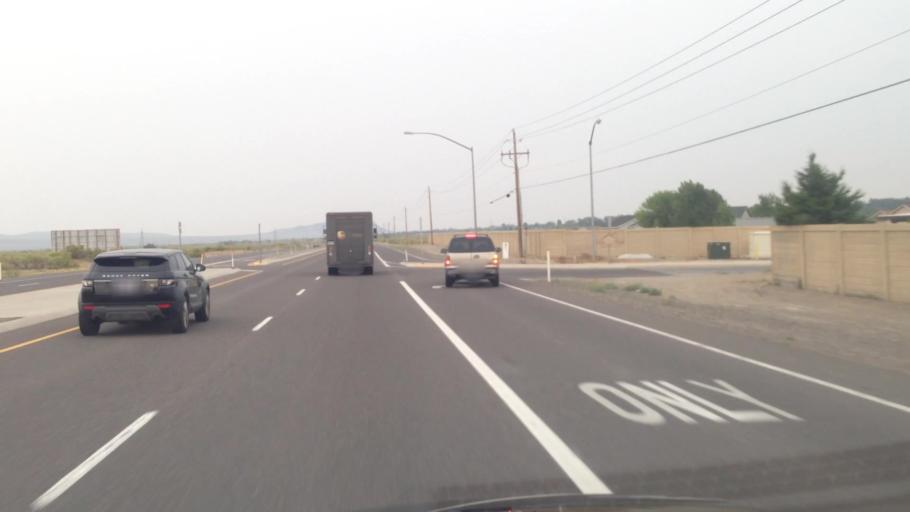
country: US
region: Nevada
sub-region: Lyon County
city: Fernley
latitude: 39.5973
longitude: -119.1919
